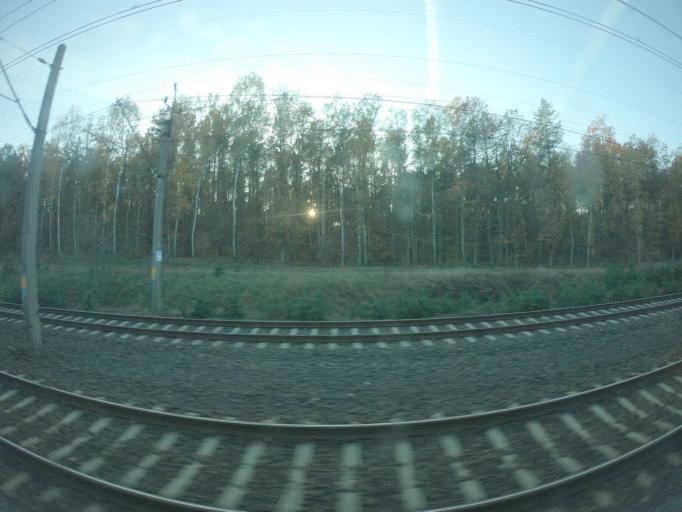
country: PL
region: Lubusz
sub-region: Powiat slubicki
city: Rzepin
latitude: 52.3173
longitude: 14.8547
